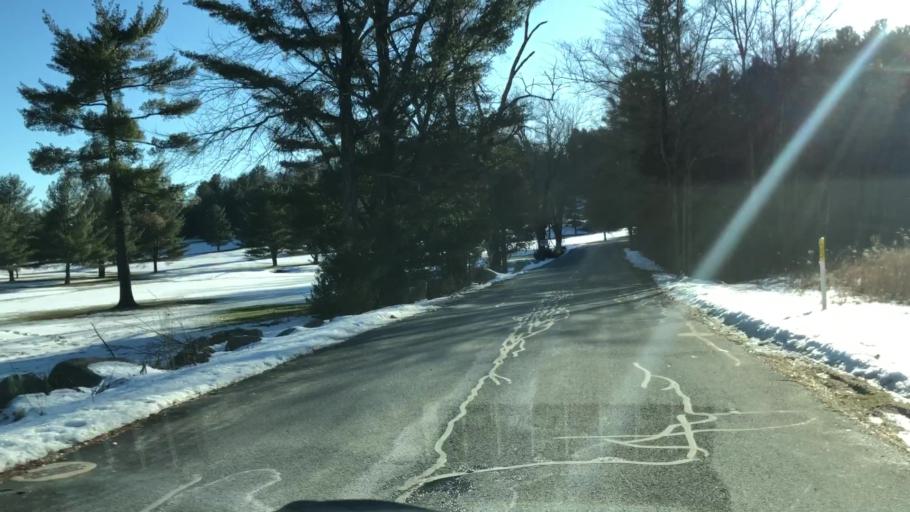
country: US
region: Massachusetts
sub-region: Hampshire County
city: Easthampton
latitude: 42.3003
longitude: -72.6668
